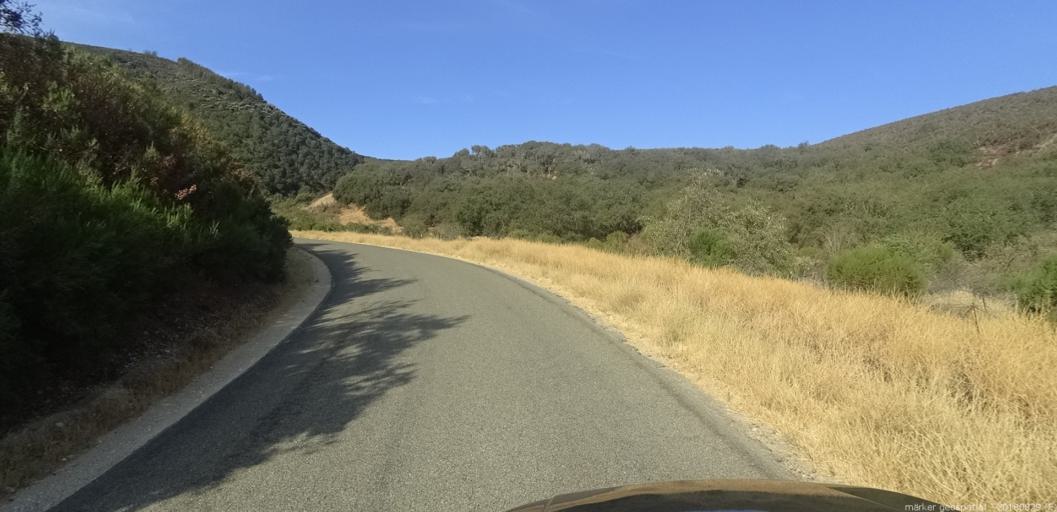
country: US
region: California
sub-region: Monterey County
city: King City
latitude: 36.0476
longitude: -121.0594
